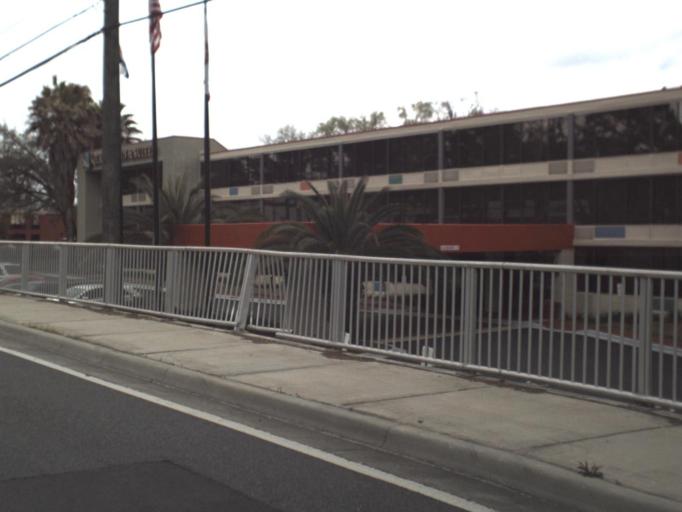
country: US
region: Florida
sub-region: Leon County
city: Tallahassee
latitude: 30.4311
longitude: -84.2463
